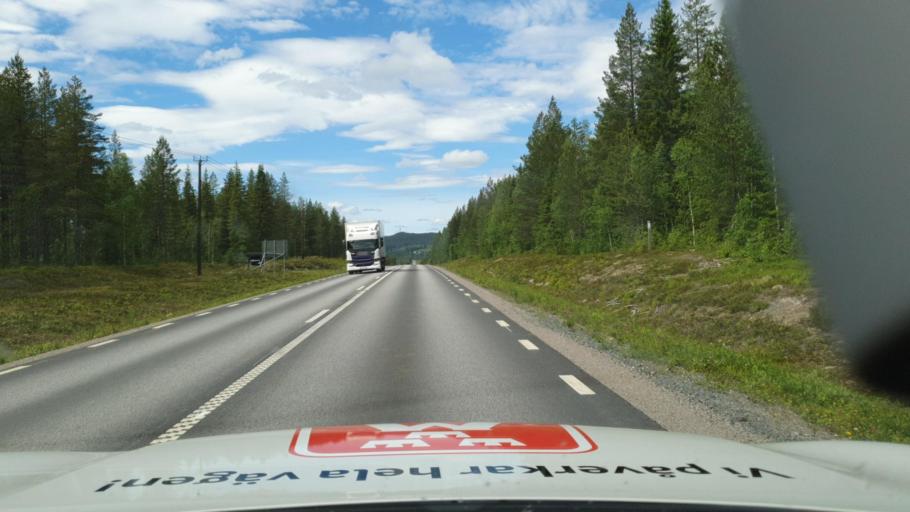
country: SE
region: Vaesterbotten
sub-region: Norsjo Kommun
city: Norsjoe
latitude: 65.2449
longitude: 19.7036
